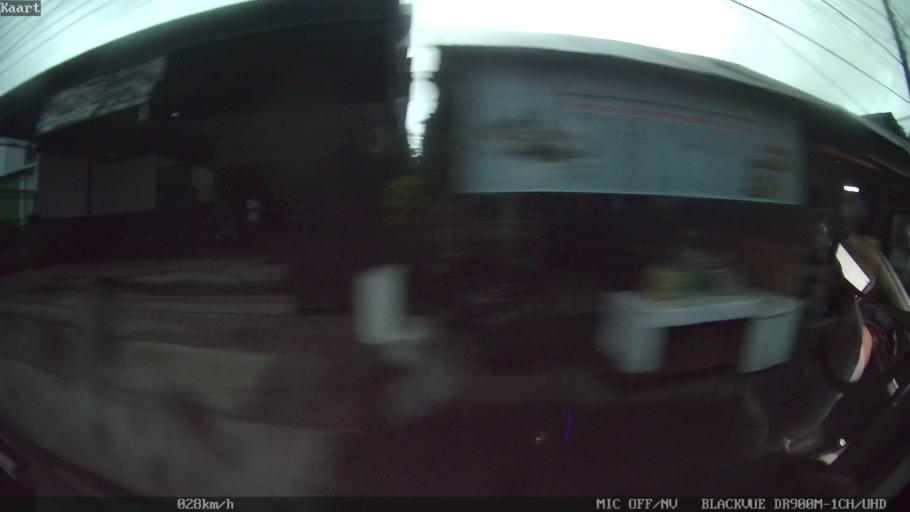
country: ID
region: Bali
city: Banjar Kayangan
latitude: -8.6183
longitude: 115.2231
